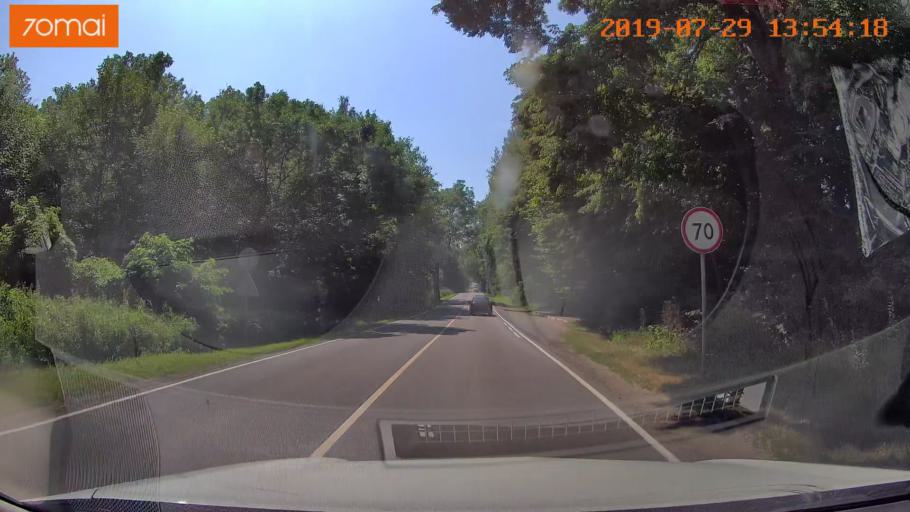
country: RU
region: Kaliningrad
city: Primorsk
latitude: 54.7243
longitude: 19.9679
